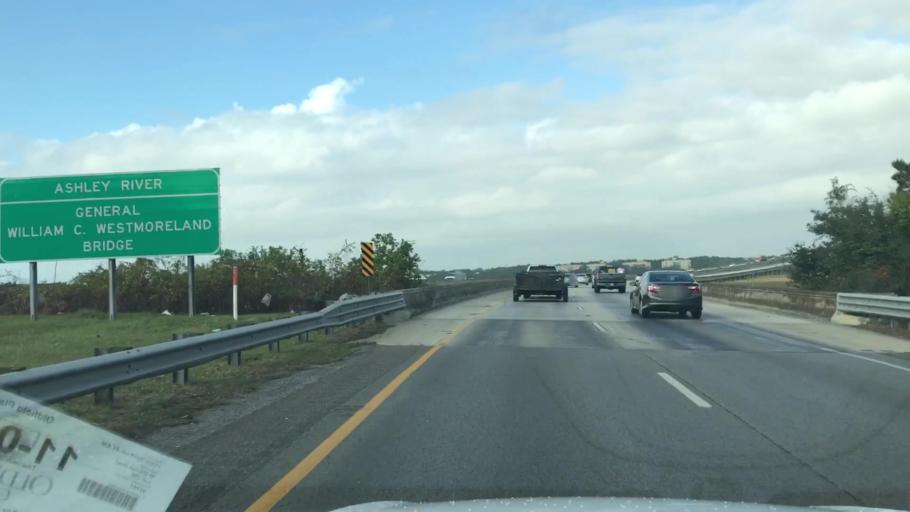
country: US
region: South Carolina
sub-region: Charleston County
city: North Charleston
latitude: 32.8285
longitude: -80.0296
